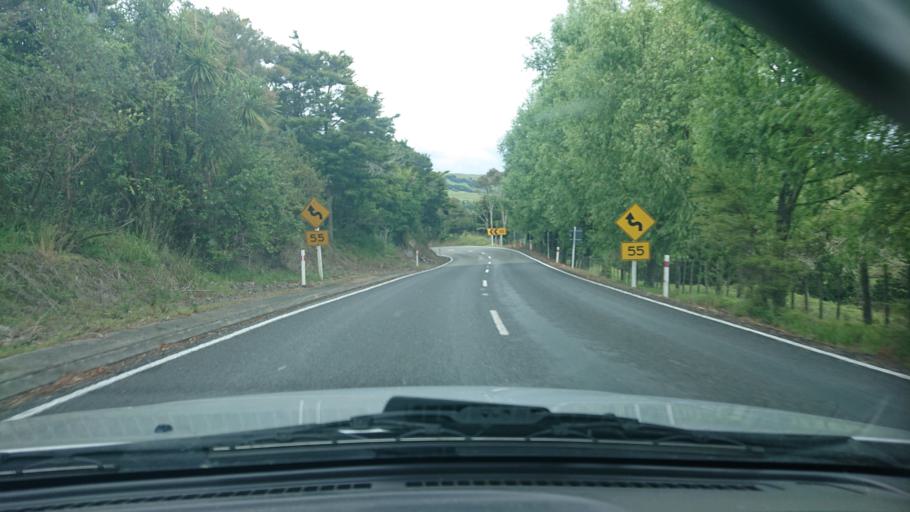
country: NZ
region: Auckland
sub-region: Auckland
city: Wellsford
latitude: -36.3684
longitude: 174.4524
